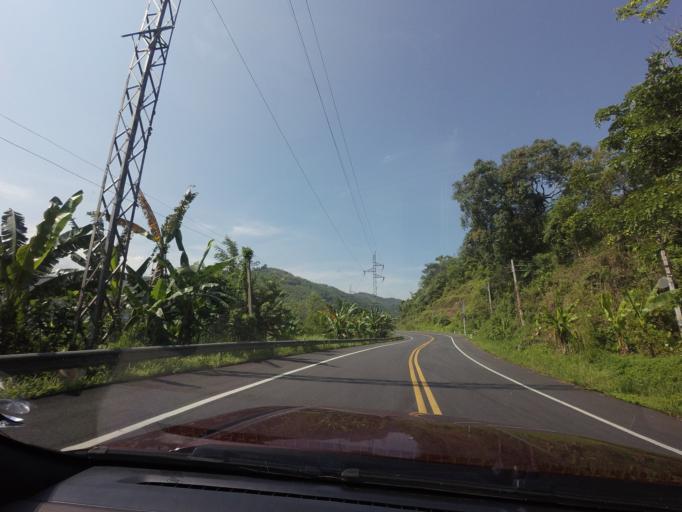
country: TH
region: Yala
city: Than To
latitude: 5.9764
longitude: 101.2008
